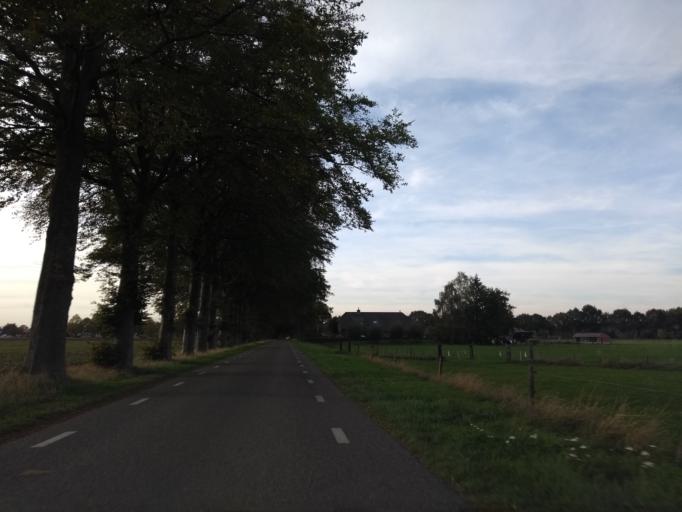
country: NL
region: Gelderland
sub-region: Gemeente Bronckhorst
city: Hengelo
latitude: 52.0458
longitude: 6.3227
